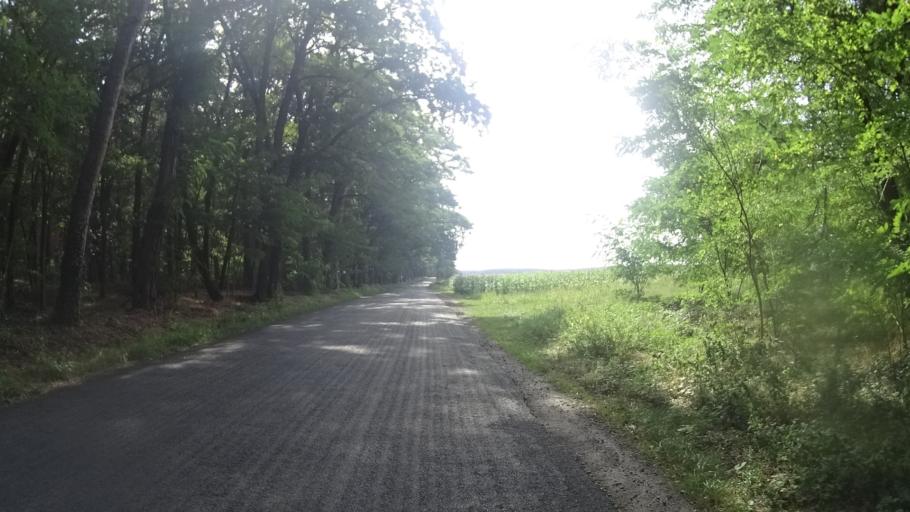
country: DE
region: Brandenburg
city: Golzow
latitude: 52.3235
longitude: 12.6762
